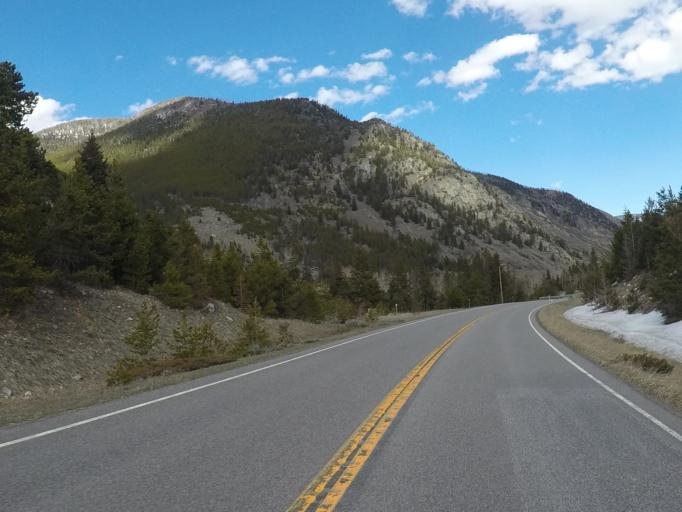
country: US
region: Montana
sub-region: Carbon County
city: Red Lodge
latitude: 45.0863
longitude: -109.3693
